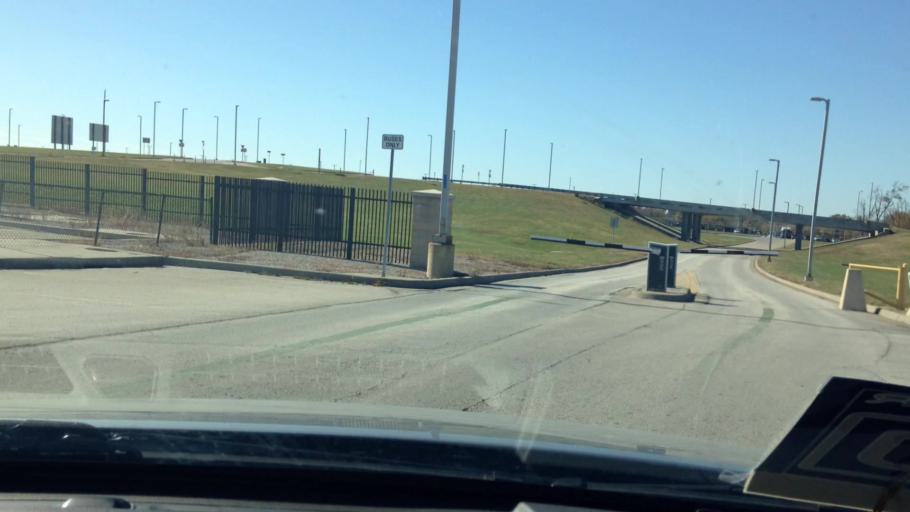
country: US
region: Missouri
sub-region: Platte County
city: Weatherby Lake
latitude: 39.3154
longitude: -94.6978
